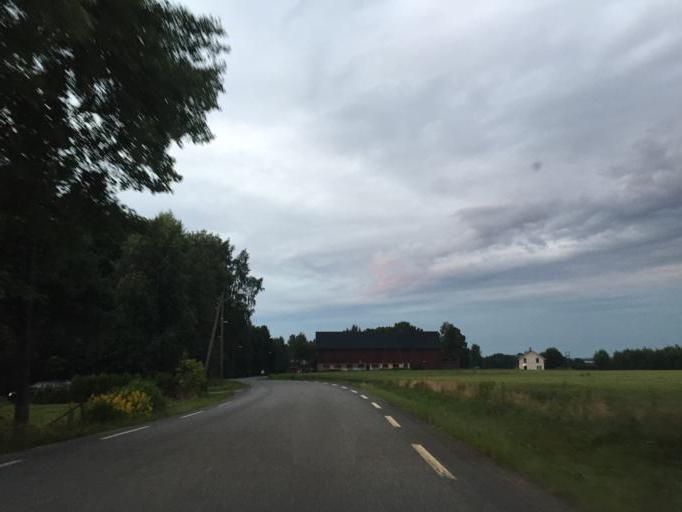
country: NO
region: Akershus
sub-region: Nes
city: Fjellfoten
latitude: 60.0930
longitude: 11.4222
